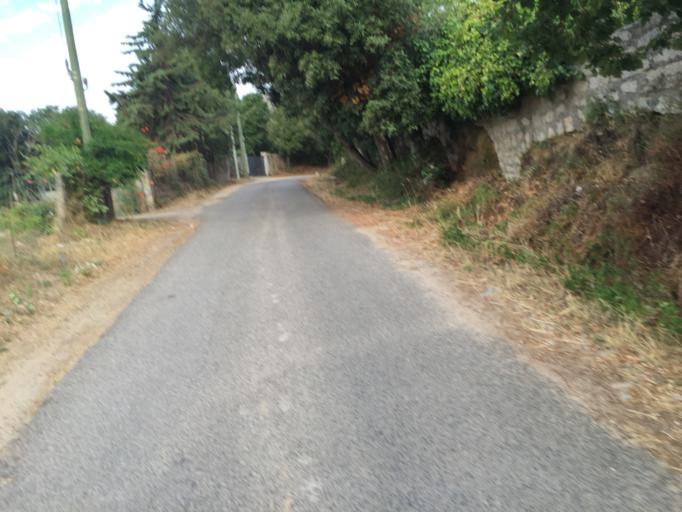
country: IT
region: Sardinia
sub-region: Provincia di Olbia-Tempio
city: Aggius
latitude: 40.9278
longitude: 9.0705
